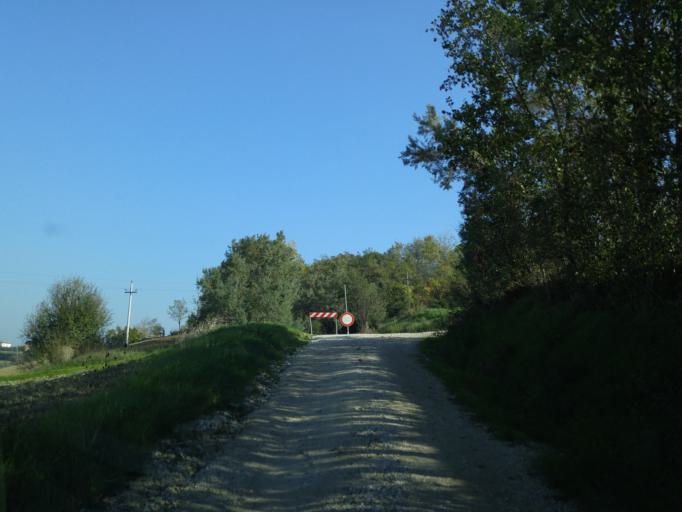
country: IT
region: The Marches
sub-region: Provincia di Pesaro e Urbino
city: Piagge
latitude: 43.7293
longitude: 12.9582
